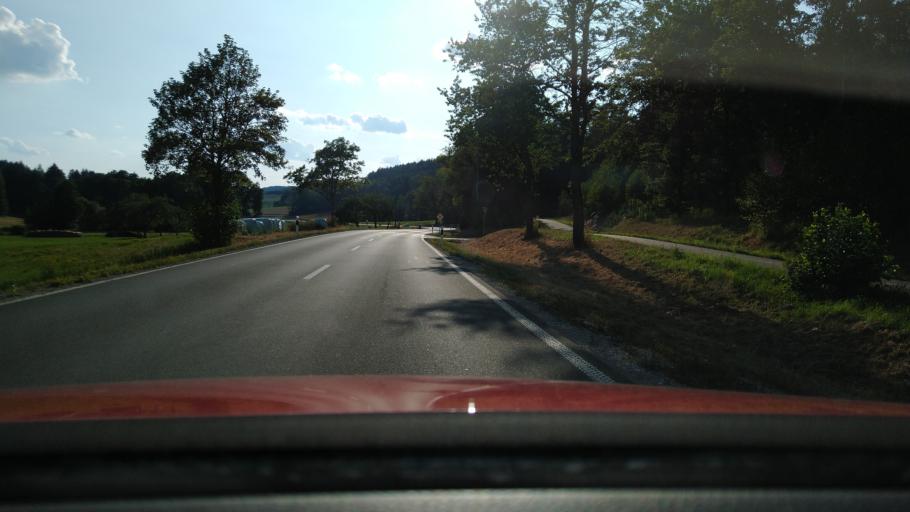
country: DE
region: Bavaria
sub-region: Upper Franconia
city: Glashutten
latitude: 49.9234
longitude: 11.4166
